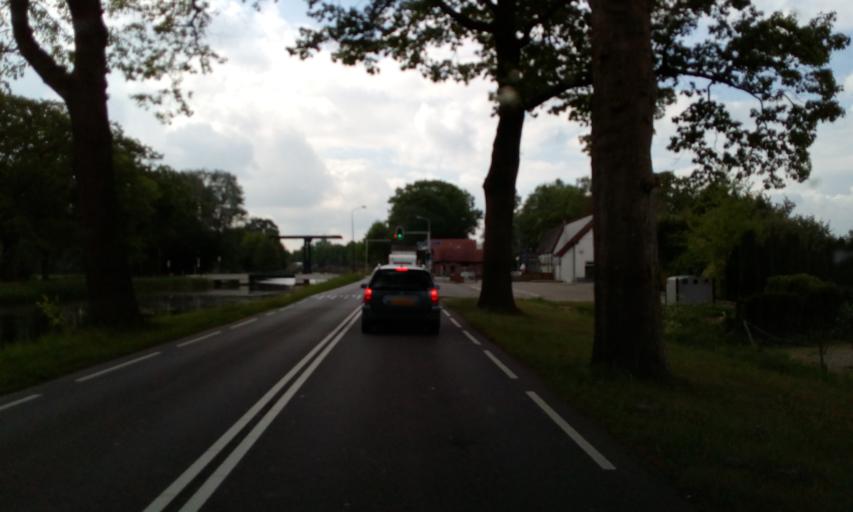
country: NL
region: Gelderland
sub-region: Gemeente Apeldoorn
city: Beekbergen
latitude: 52.1669
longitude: 5.9993
